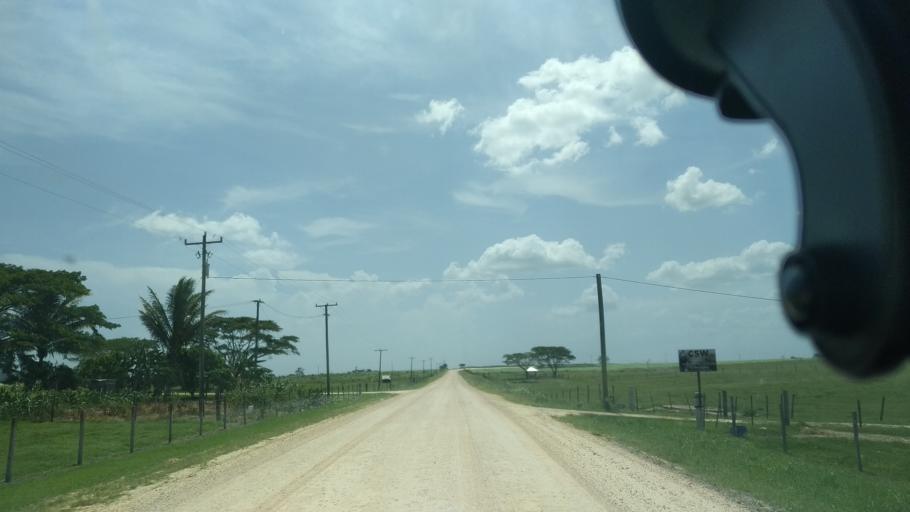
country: BZ
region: Cayo
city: San Ignacio
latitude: 17.3148
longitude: -89.0409
